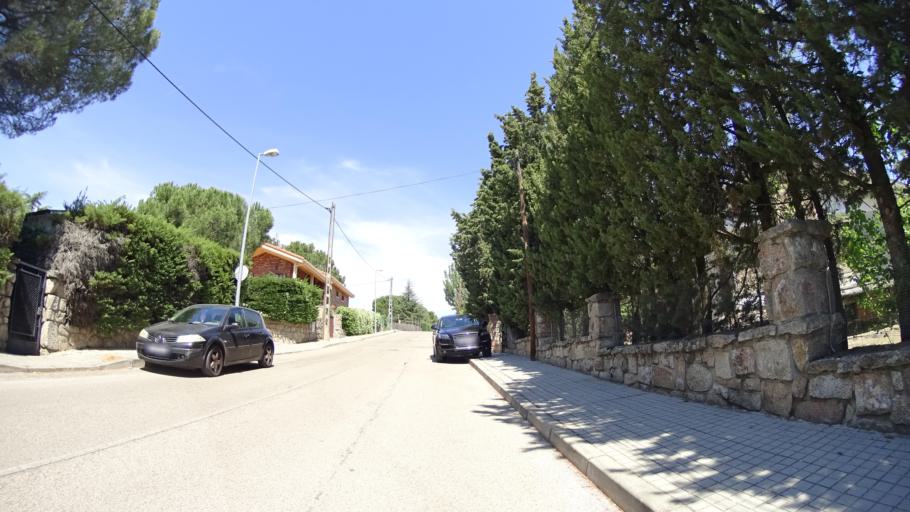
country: ES
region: Madrid
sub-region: Provincia de Madrid
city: Colmenarejo
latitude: 40.5549
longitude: -4.0052
